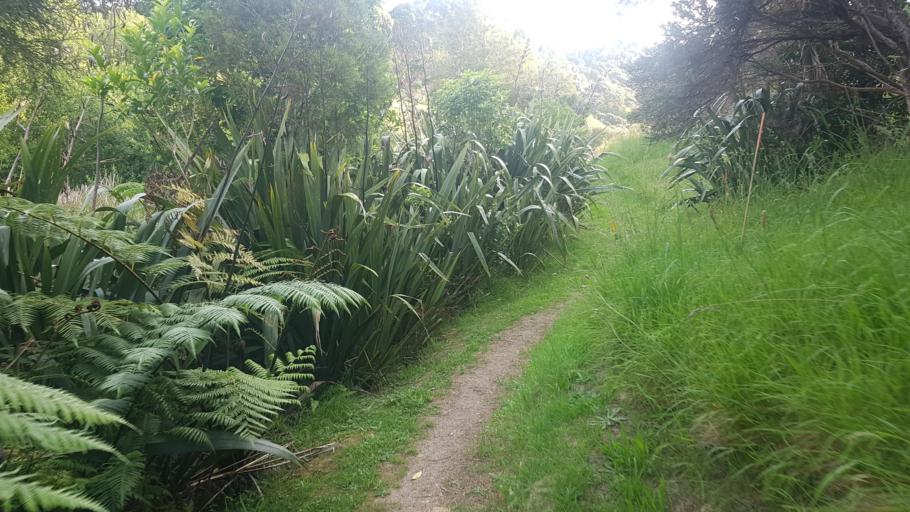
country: NZ
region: Auckland
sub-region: Auckland
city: Pakuranga
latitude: -36.7797
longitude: 175.0009
